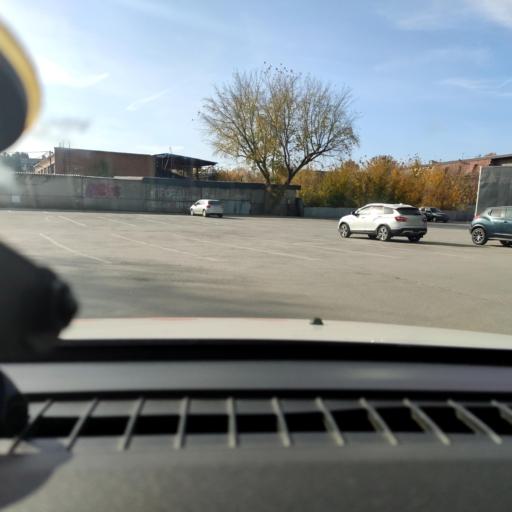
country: RU
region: Samara
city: Smyshlyayevka
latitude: 53.2291
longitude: 50.3016
